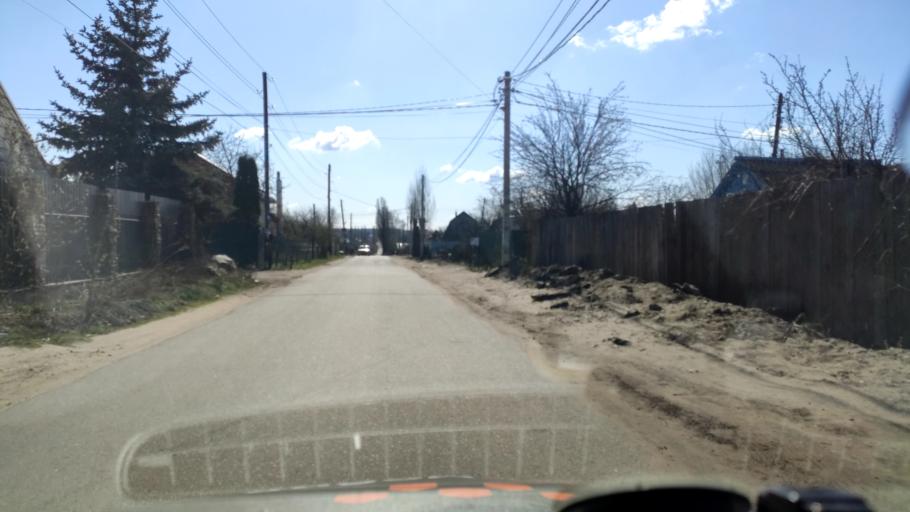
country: RU
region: Voronezj
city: Shilovo
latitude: 51.5990
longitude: 39.1458
